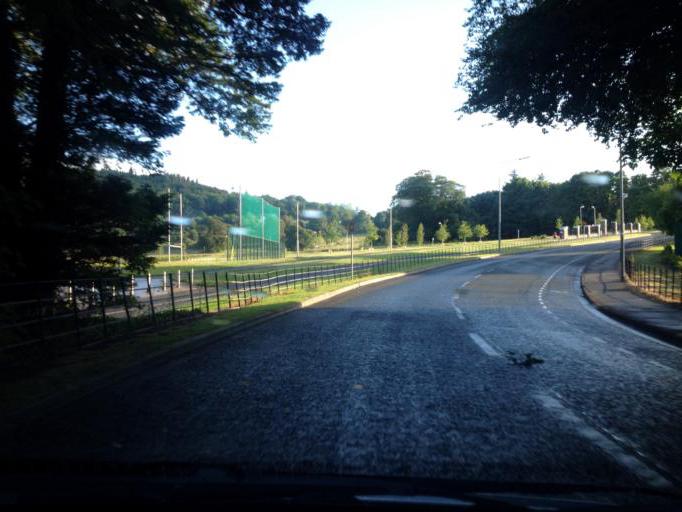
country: IE
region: Connaught
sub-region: Sligo
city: Sligo
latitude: 54.2628
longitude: -8.4473
